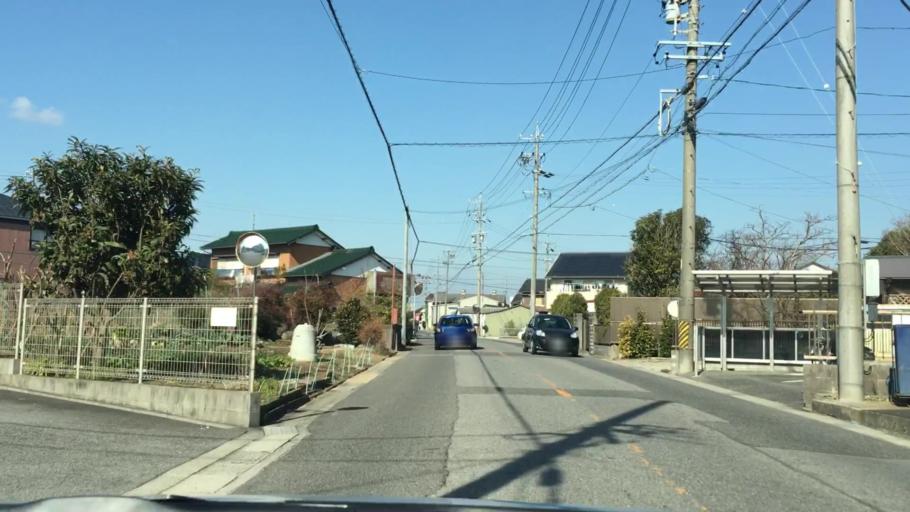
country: JP
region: Aichi
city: Anjo
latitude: 34.9743
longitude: 137.1203
